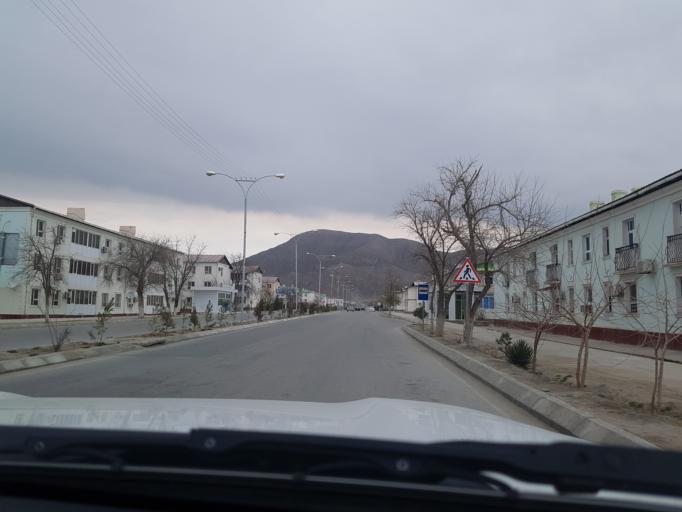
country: TM
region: Balkan
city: Balkanabat
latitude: 39.5106
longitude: 54.3466
